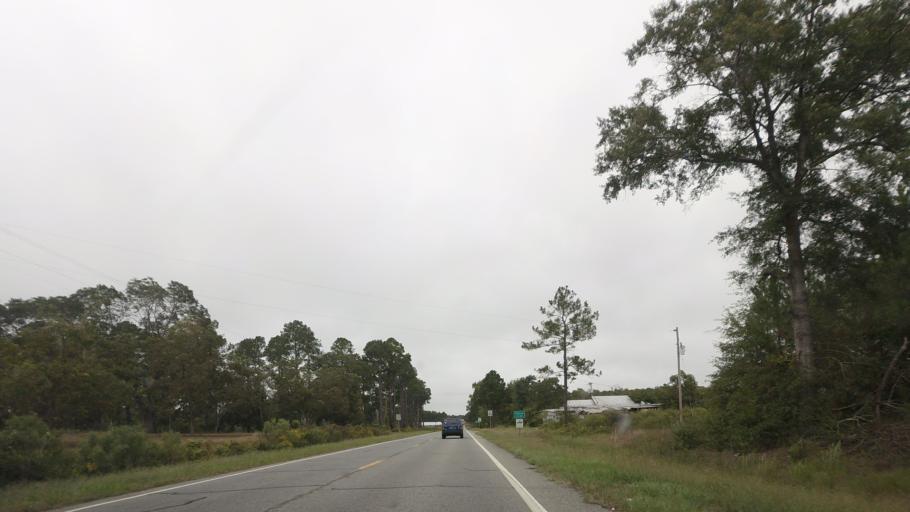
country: US
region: Georgia
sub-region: Irwin County
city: Ocilla
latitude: 31.5662
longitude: -83.2529
